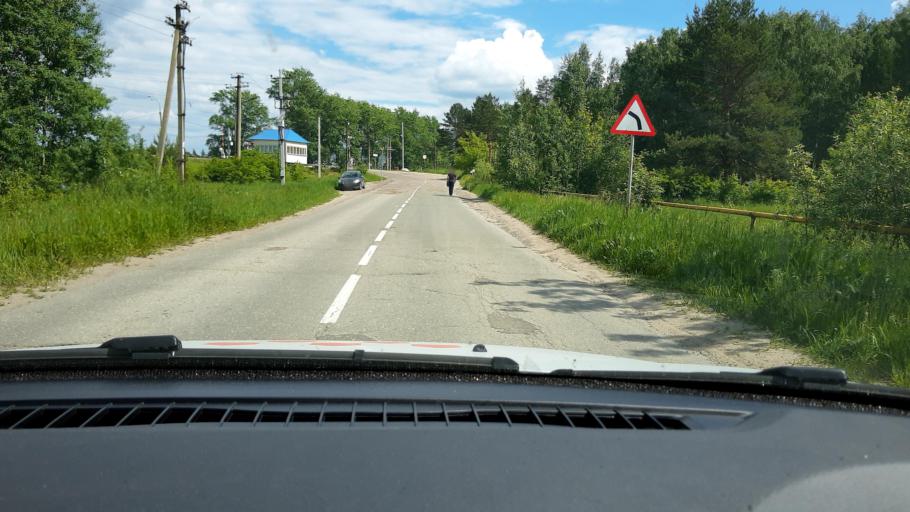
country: RU
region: Nizjnij Novgorod
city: Kstovo
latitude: 56.1680
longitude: 44.1732
